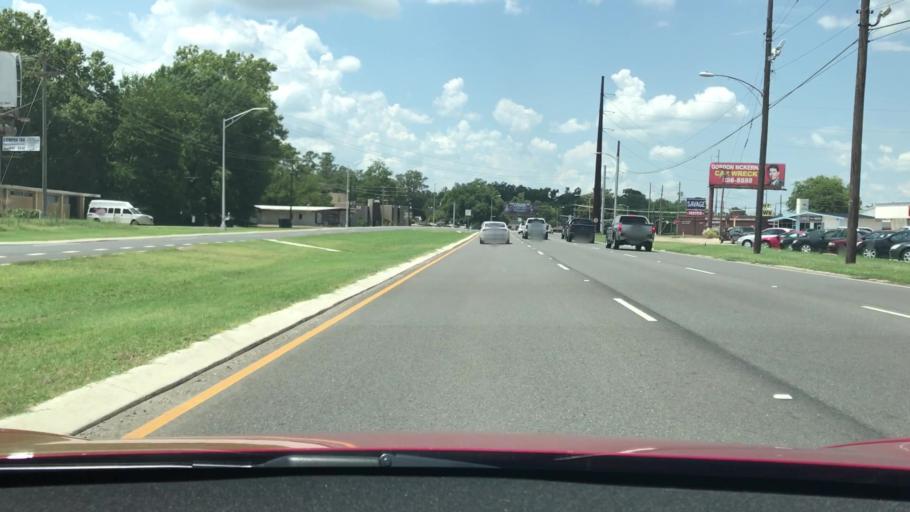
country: US
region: Louisiana
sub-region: Bossier Parish
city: Bossier City
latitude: 32.4822
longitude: -93.7232
